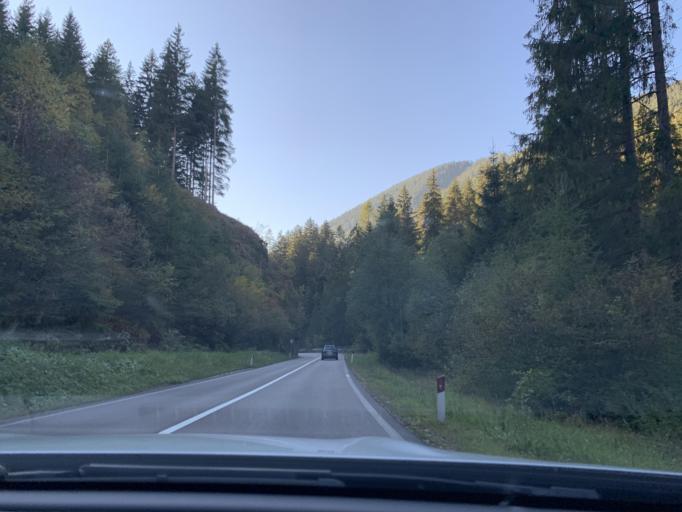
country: IT
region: Trentino-Alto Adige
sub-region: Bolzano
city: Nova Levante
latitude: 46.4255
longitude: 11.5137
